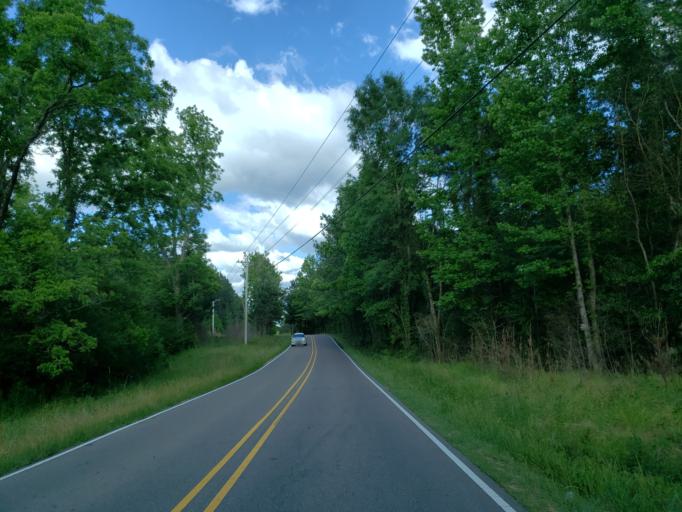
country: US
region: Mississippi
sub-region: Lamar County
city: West Hattiesburg
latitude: 31.2736
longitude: -89.3815
